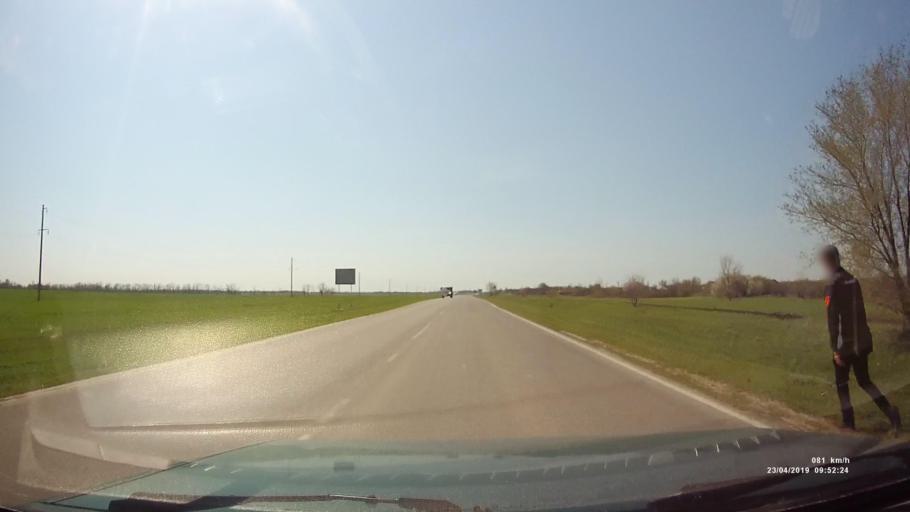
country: RU
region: Rostov
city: Orlovskiy
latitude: 46.8449
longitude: 42.0456
